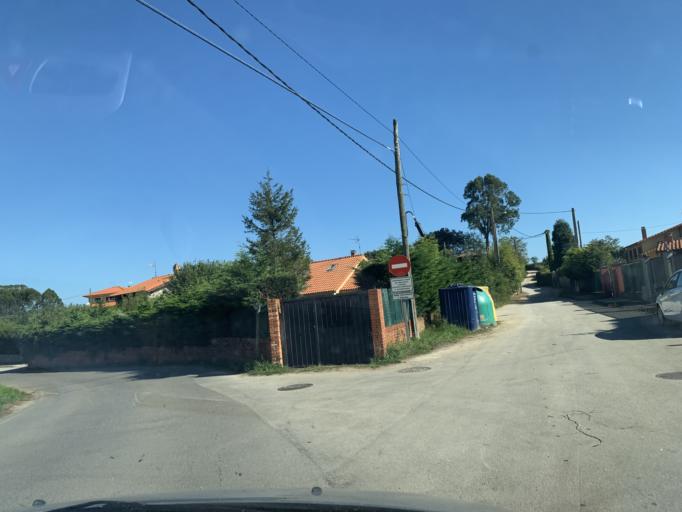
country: ES
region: Asturias
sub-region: Province of Asturias
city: Llanes
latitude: 43.4258
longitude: -4.7799
